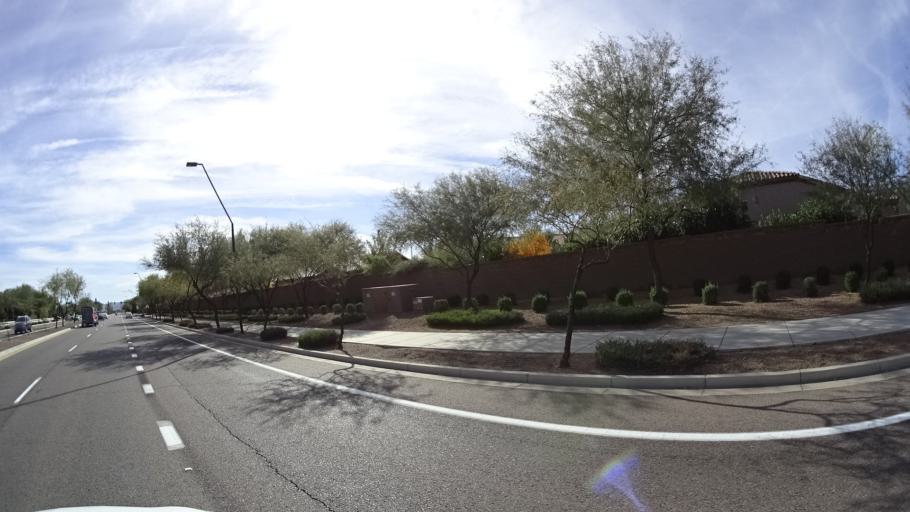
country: US
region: Arizona
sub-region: Maricopa County
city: Queen Creek
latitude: 33.2543
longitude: -111.6860
